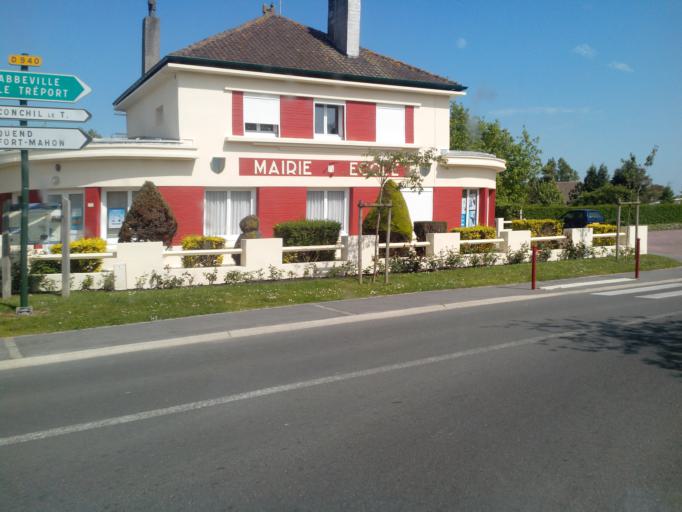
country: FR
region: Nord-Pas-de-Calais
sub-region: Departement du Pas-de-Calais
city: Verton
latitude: 50.3795
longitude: 1.6528
